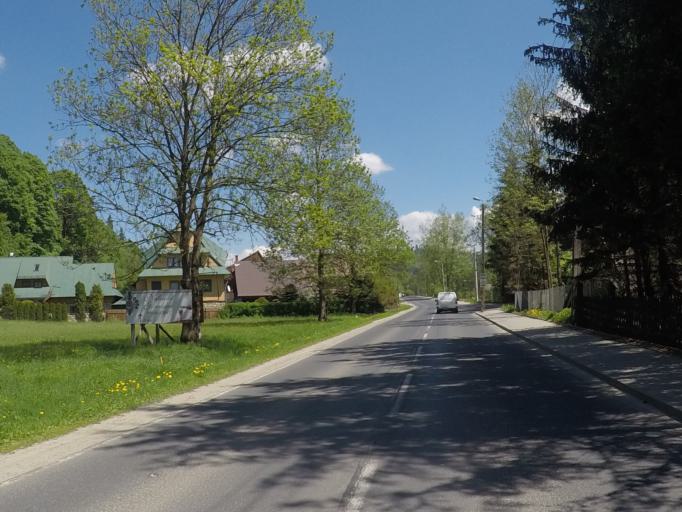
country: PL
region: Lesser Poland Voivodeship
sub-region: Powiat tatrzanski
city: Poronin
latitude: 49.3313
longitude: 20.0263
